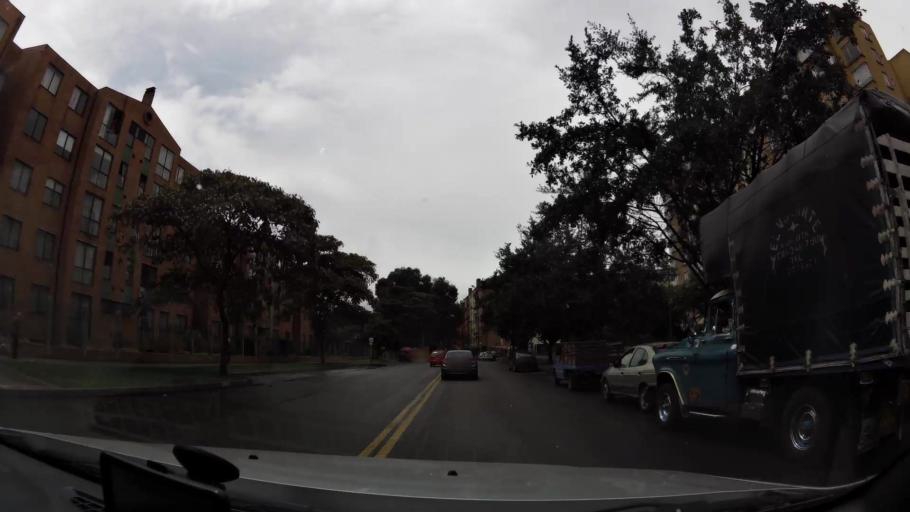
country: CO
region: Bogota D.C.
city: Bogota
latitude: 4.6490
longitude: -74.1084
